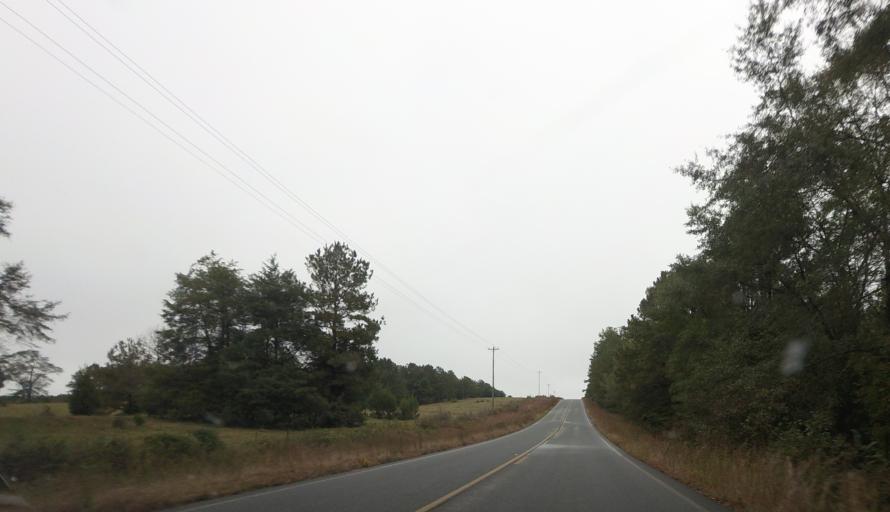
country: US
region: Georgia
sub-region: Marion County
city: Buena Vista
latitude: 32.3847
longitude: -84.4332
